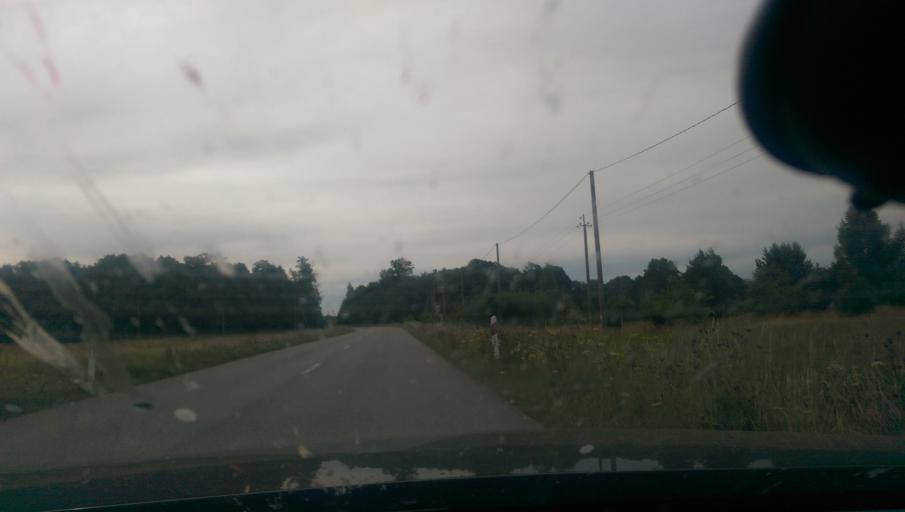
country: LT
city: Priekule
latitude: 55.5999
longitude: 21.4017
